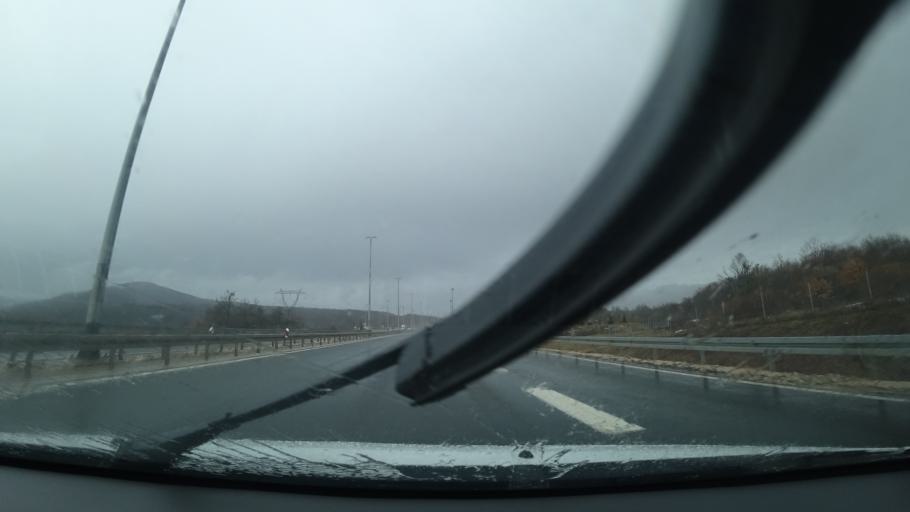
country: HR
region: Licko-Senjska
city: Gospic
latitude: 44.6221
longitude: 15.4379
